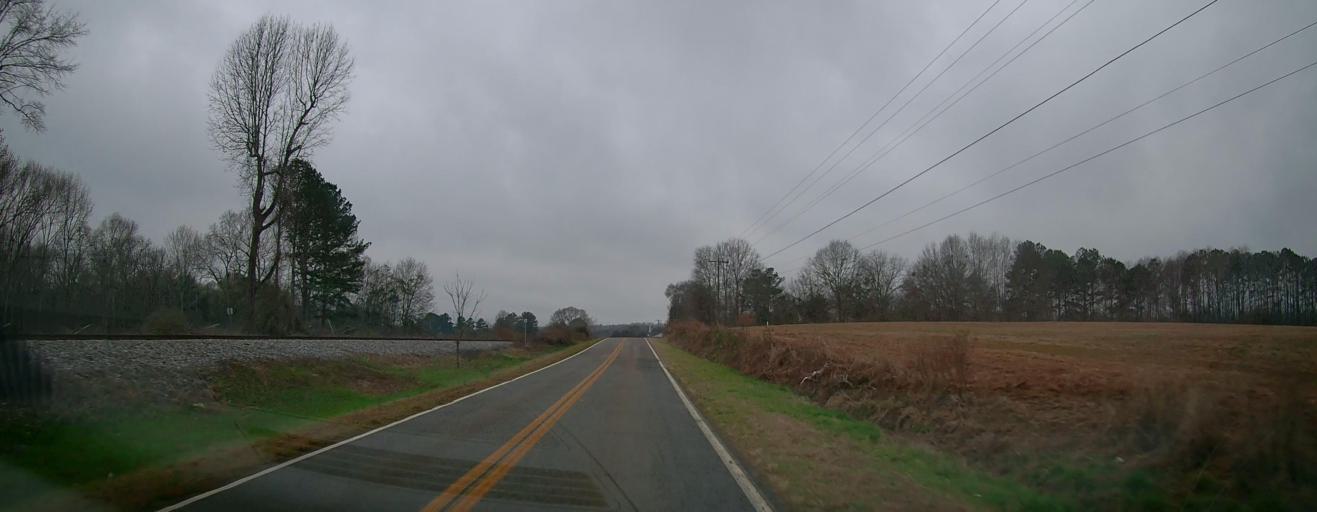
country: US
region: Georgia
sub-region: Lamar County
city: Barnesville
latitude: 33.0747
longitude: -84.1025
